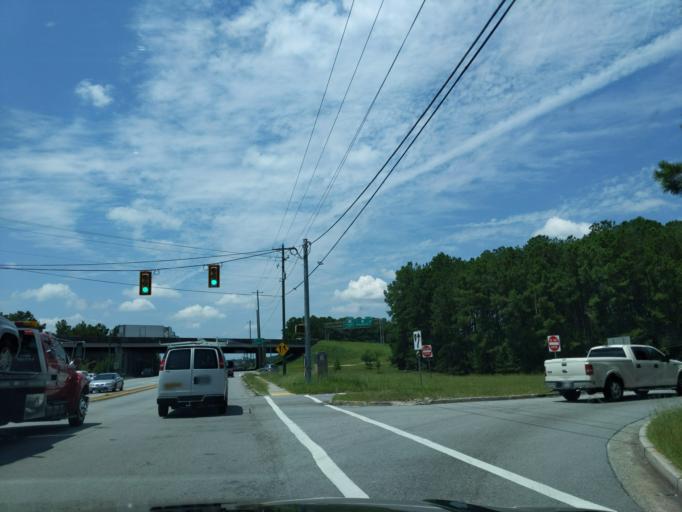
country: US
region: South Carolina
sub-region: Richland County
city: Dentsville
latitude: 34.0749
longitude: -80.9464
